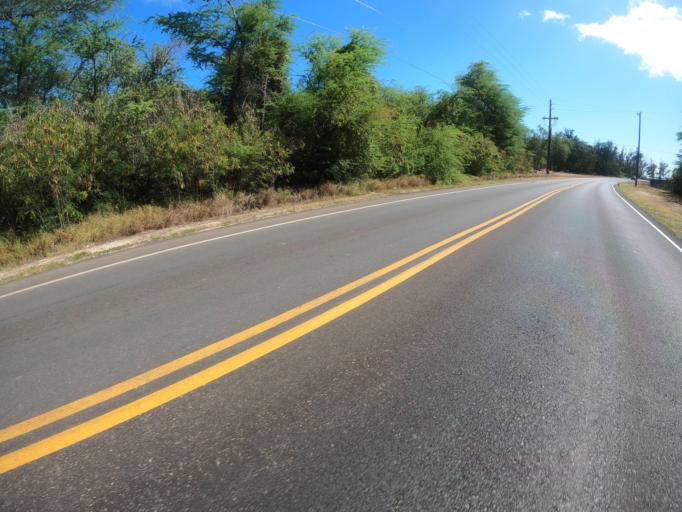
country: US
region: Hawaii
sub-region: Honolulu County
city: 'Ewa Villages
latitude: 21.3038
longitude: -158.0574
